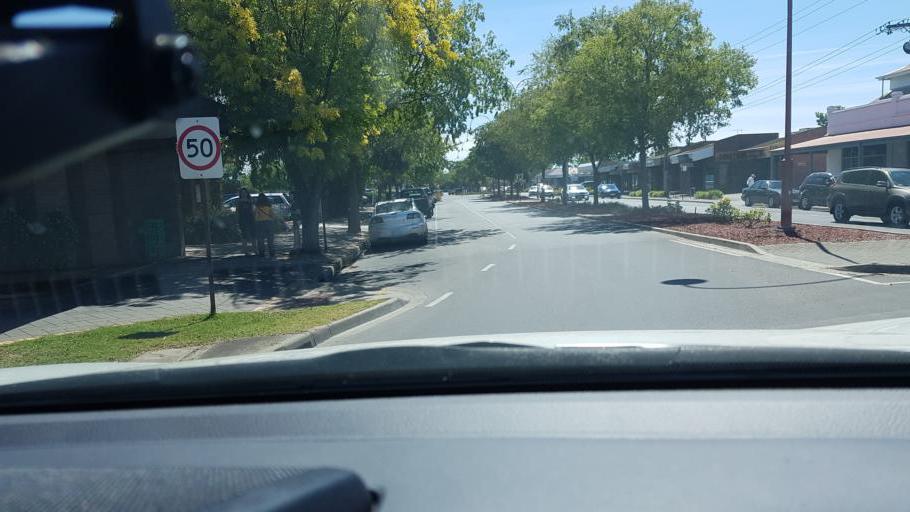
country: AU
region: Victoria
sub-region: Horsham
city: Horsham
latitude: -36.7166
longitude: 142.1971
